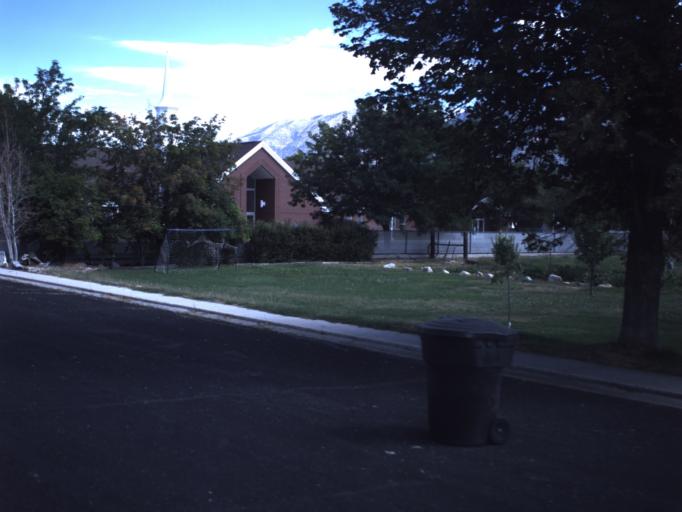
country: US
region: Utah
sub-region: Box Elder County
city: Honeyville
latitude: 41.6151
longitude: -112.1270
